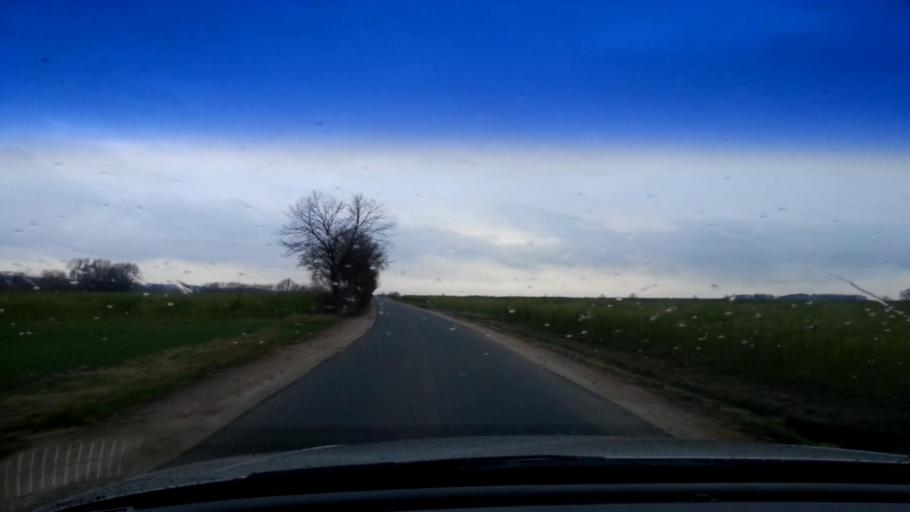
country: DE
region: Bavaria
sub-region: Upper Franconia
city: Frensdorf
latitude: 49.8233
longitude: 10.8714
